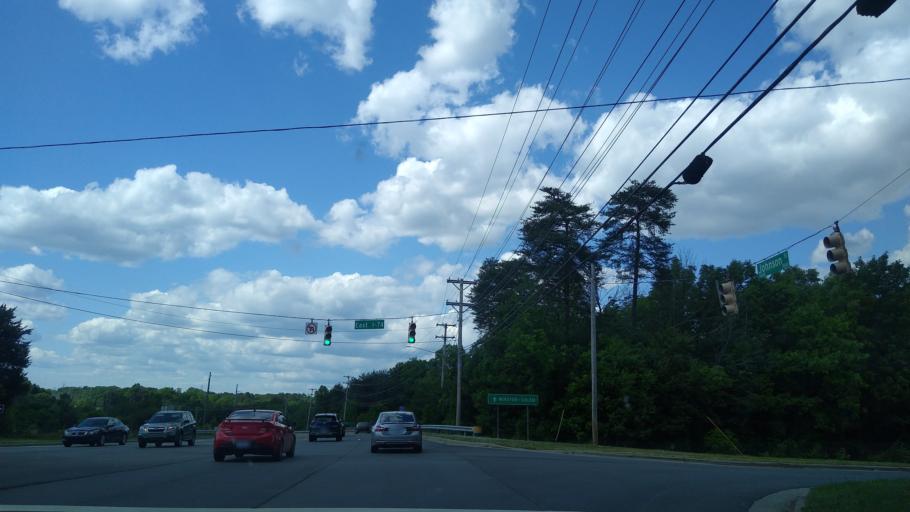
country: US
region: North Carolina
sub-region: Guilford County
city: High Point
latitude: 36.0081
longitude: -80.0099
